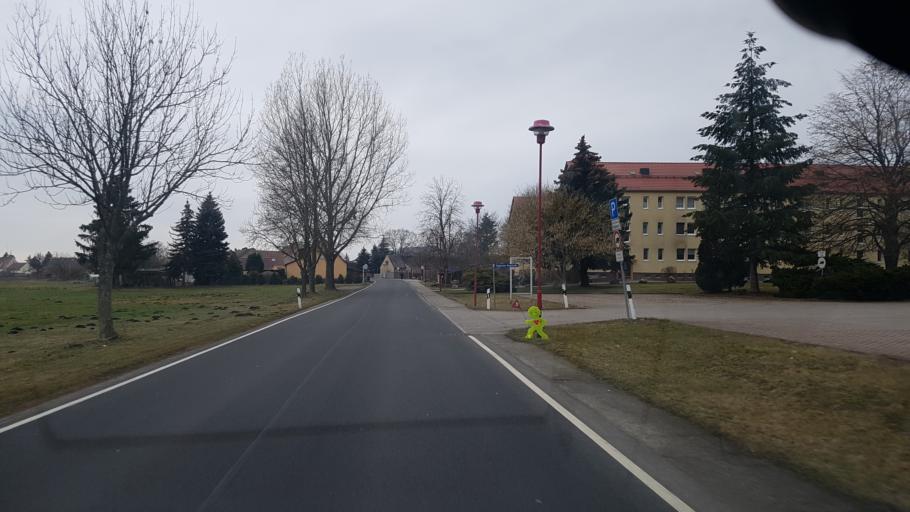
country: DE
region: Brandenburg
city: Heinersbruck
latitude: 51.7064
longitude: 14.4658
